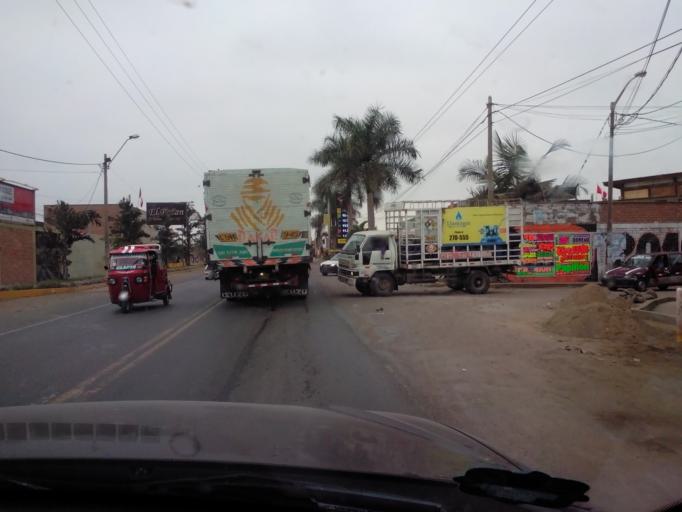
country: PE
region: Ica
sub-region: Provincia de Chincha
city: Chincha Alta
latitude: -13.4328
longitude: -76.1344
